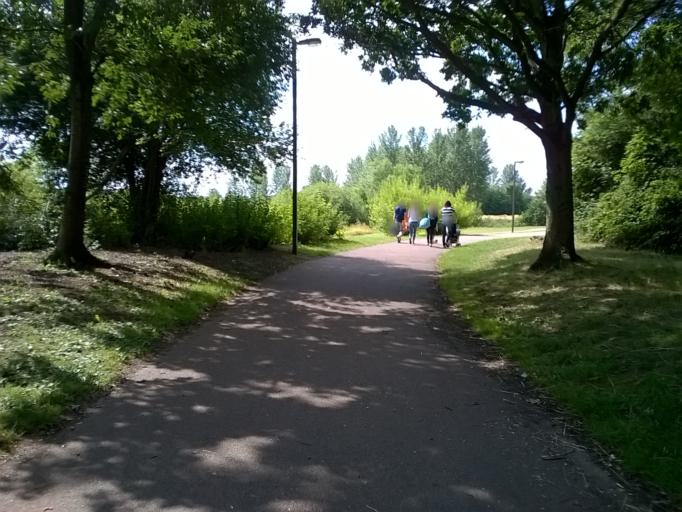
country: GB
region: England
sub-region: Milton Keynes
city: Broughton
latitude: 52.0545
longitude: -0.7239
